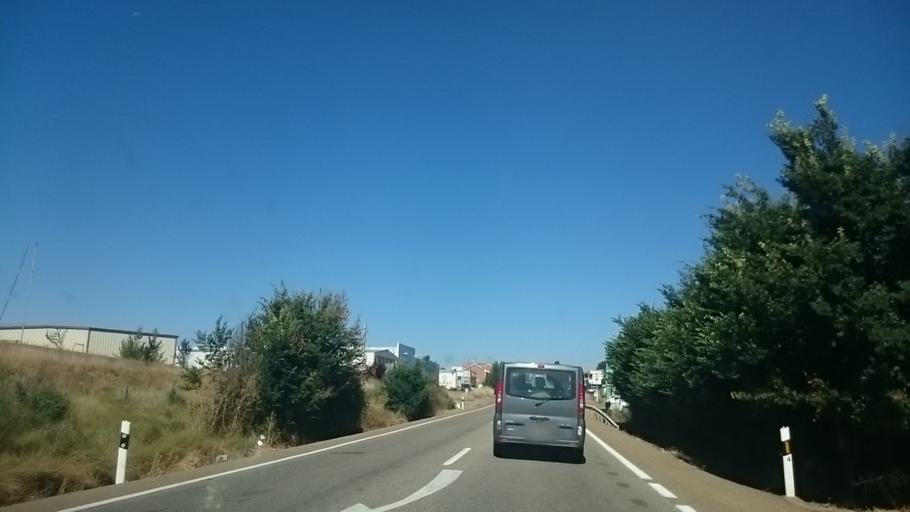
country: ES
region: Castille and Leon
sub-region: Provincia de Leon
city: Valdefresno
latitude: 42.5667
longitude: -5.5027
